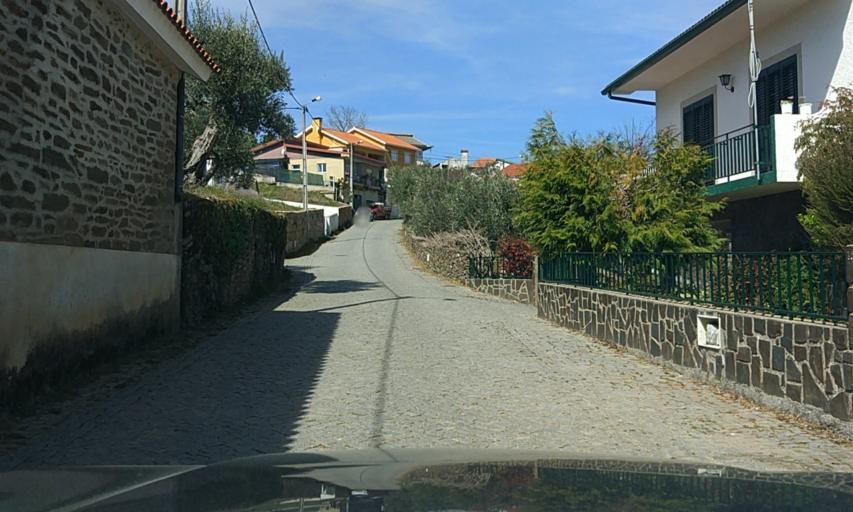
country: PT
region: Vila Real
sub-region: Sabrosa
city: Sabrosa
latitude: 41.3045
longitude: -7.5592
